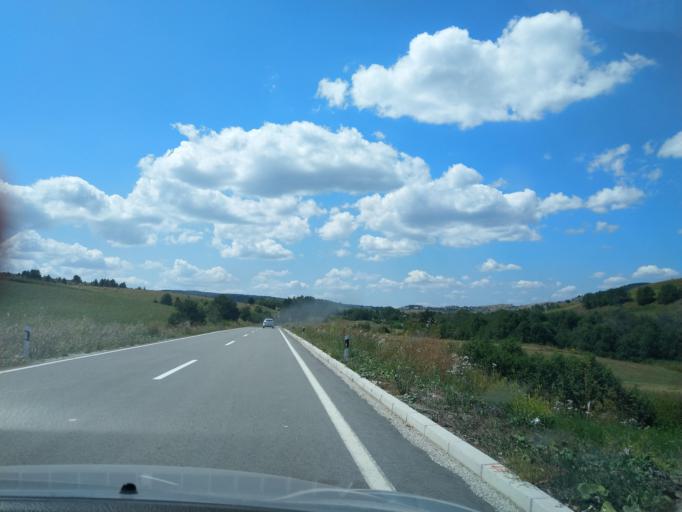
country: RS
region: Central Serbia
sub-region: Zlatiborski Okrug
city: Sjenica
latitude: 43.3276
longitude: 19.8889
